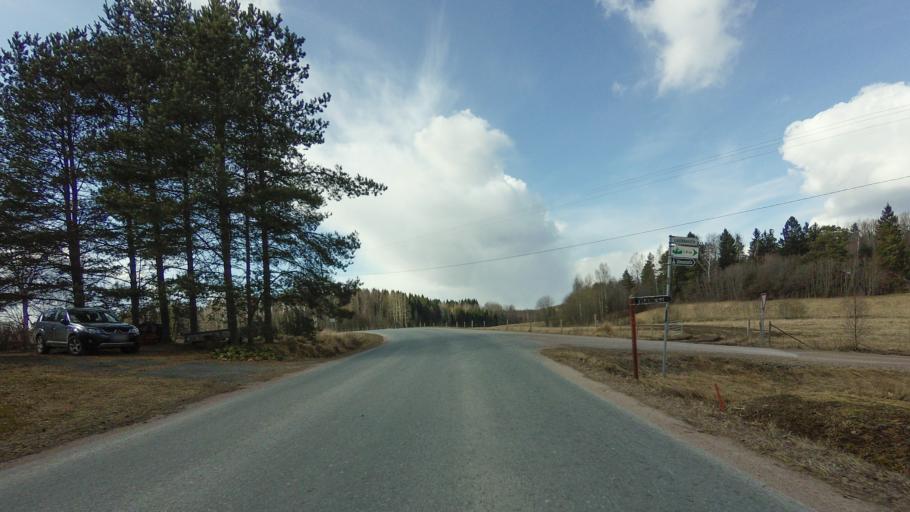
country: FI
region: Varsinais-Suomi
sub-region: Salo
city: Suomusjaervi
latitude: 60.3455
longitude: 23.6974
